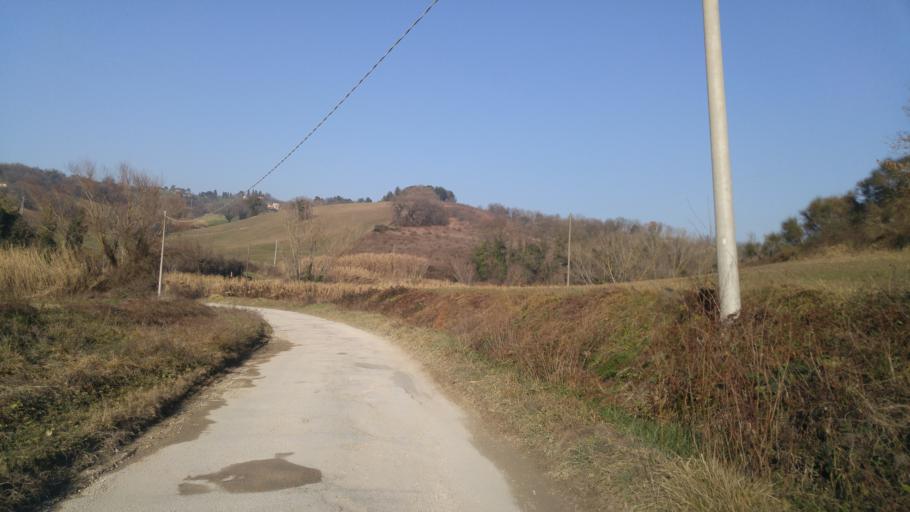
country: IT
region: The Marches
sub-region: Provincia di Pesaro e Urbino
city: Cuccurano
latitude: 43.8152
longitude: 12.9343
